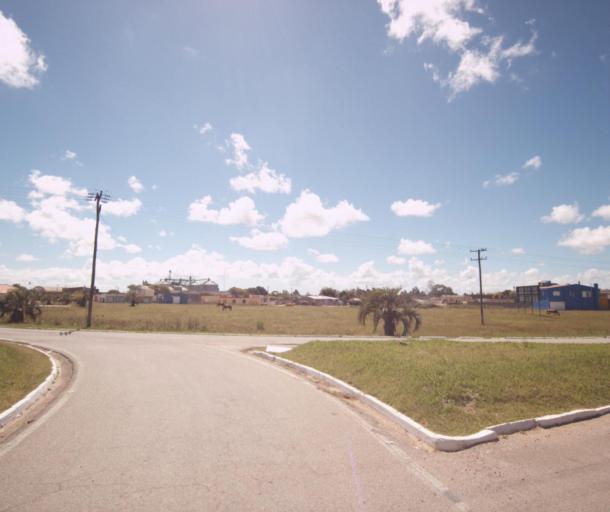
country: BR
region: Rio Grande do Sul
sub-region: Santa Vitoria Do Palmar
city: Santa Vitoria do Palmar
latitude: -33.5306
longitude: -53.3452
